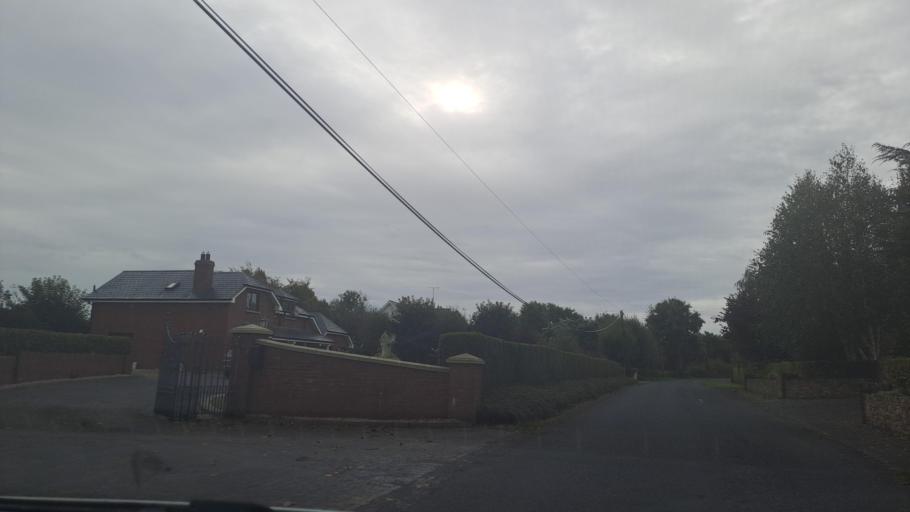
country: IE
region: Ulster
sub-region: County Monaghan
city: Carrickmacross
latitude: 53.9817
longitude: -6.7563
